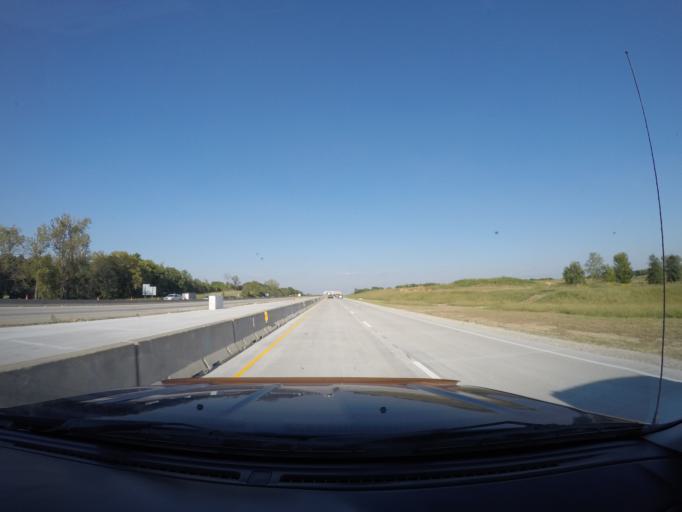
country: US
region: Kansas
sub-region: Wyandotte County
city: Bonner Springs
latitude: 39.1010
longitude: -94.8634
